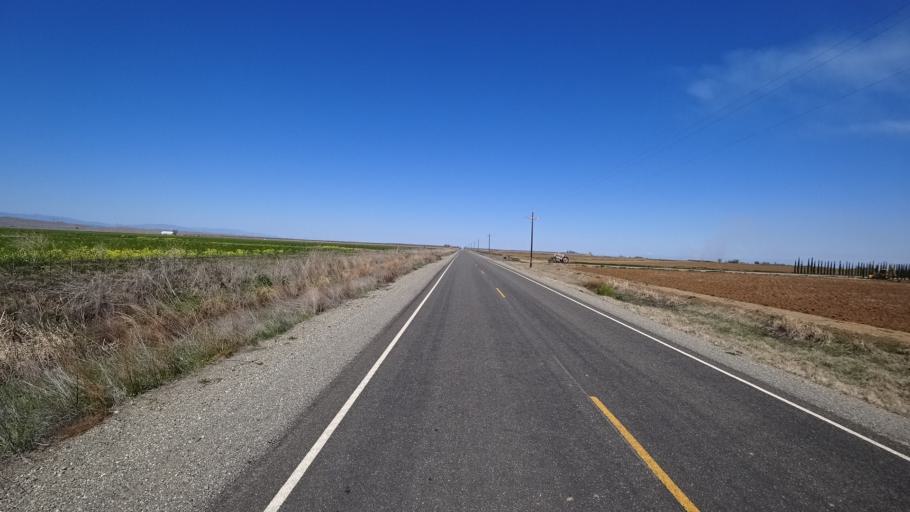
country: US
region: California
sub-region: Glenn County
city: Willows
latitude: 39.4283
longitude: -122.2486
